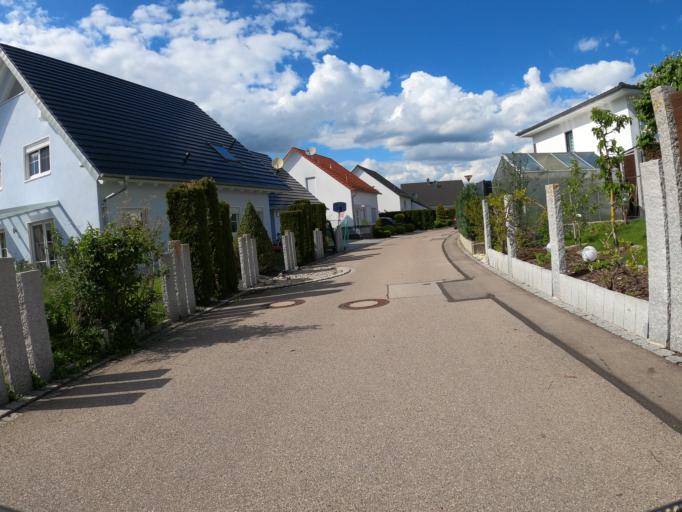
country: DE
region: Bavaria
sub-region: Swabia
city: Bubesheim
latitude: 48.4348
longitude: 10.2596
